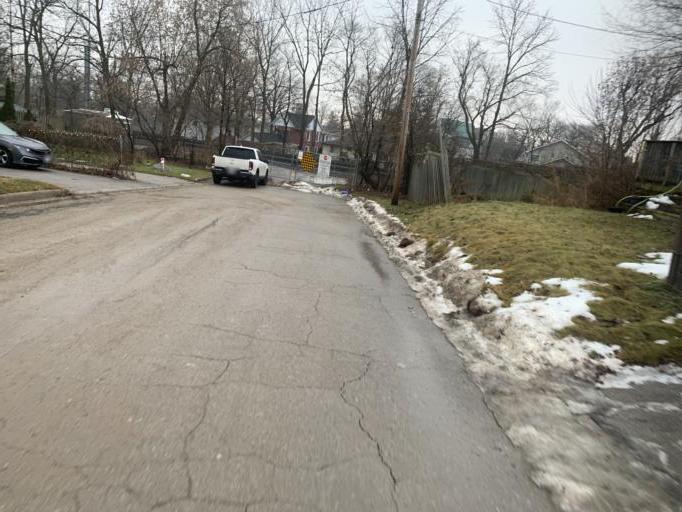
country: CA
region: Ontario
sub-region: Halton
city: Milton
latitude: 43.6538
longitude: -79.9293
